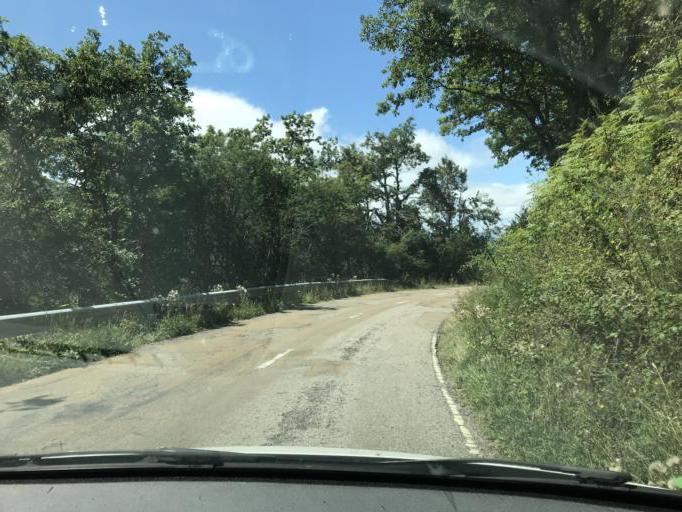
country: ES
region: Castille and Leon
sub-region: Provincia de Palencia
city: Polentinos
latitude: 43.0559
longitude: -4.4628
